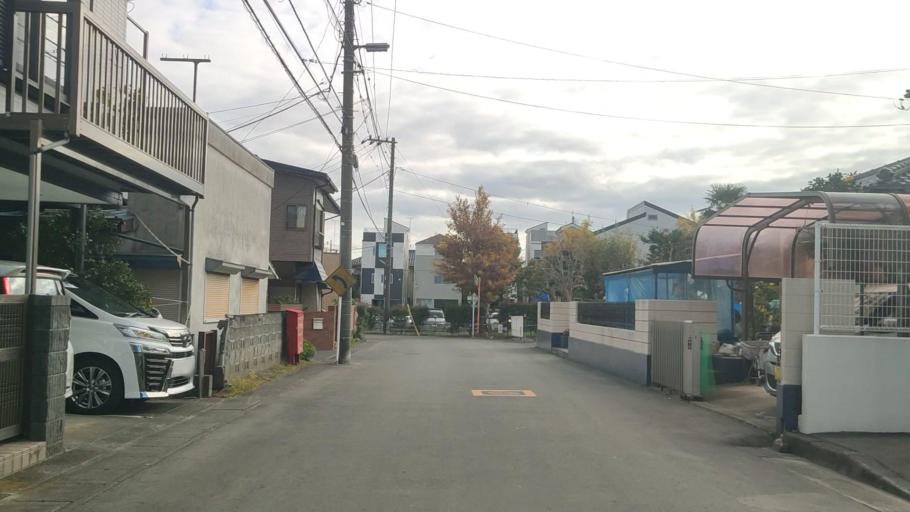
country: JP
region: Kanagawa
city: Minami-rinkan
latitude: 35.4944
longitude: 139.4337
